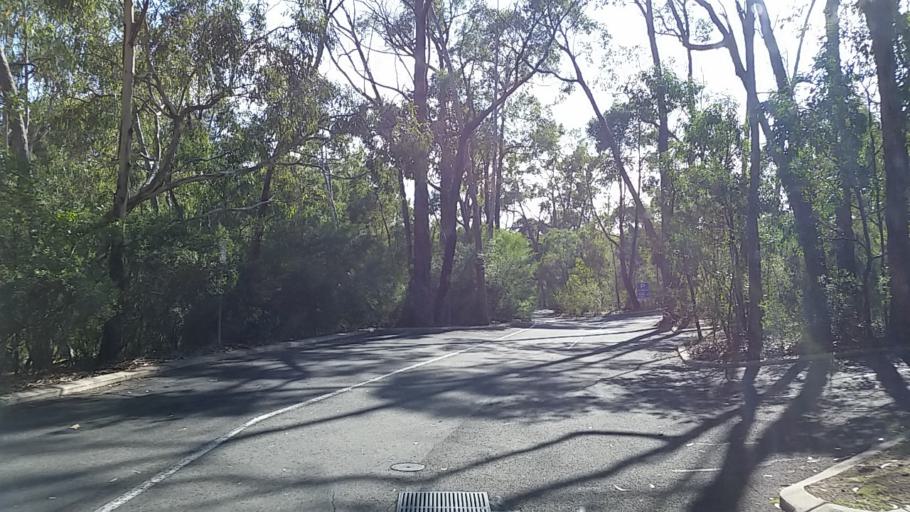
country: AU
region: South Australia
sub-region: Adelaide Hills
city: Crafers
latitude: -34.9666
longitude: 138.6969
